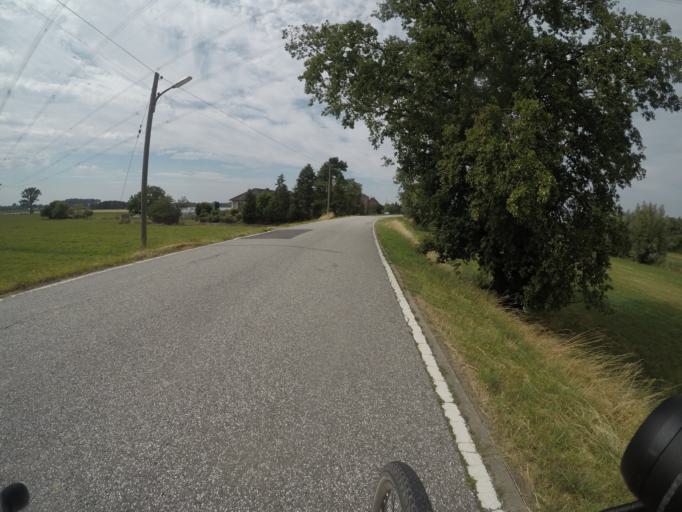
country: DE
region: Schleswig-Holstein
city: Oststeinbek
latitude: 53.4701
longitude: 10.1394
